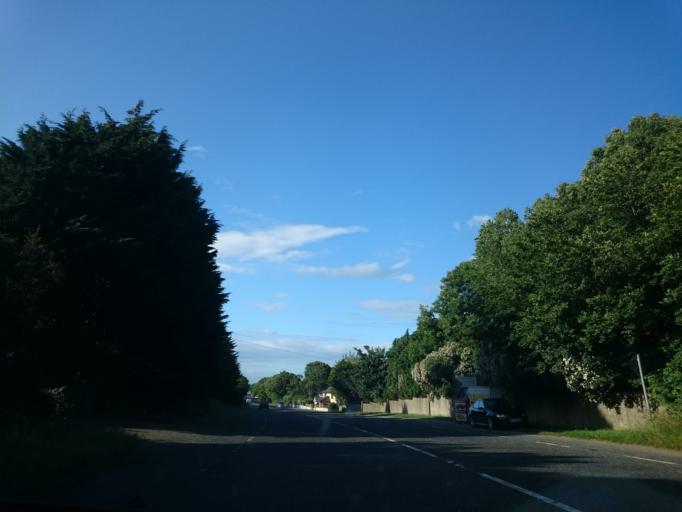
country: IE
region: Leinster
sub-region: Loch Garman
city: Loch Garman
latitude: 52.2962
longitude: -6.4602
